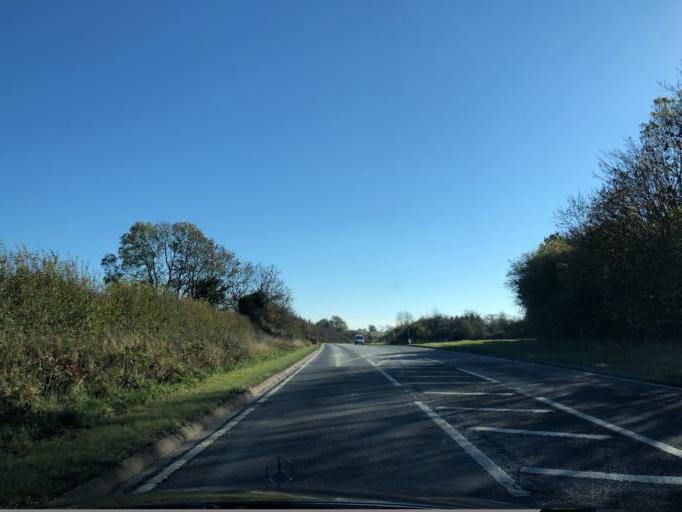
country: GB
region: England
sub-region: Warwickshire
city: Southam
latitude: 52.2320
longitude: -1.3902
